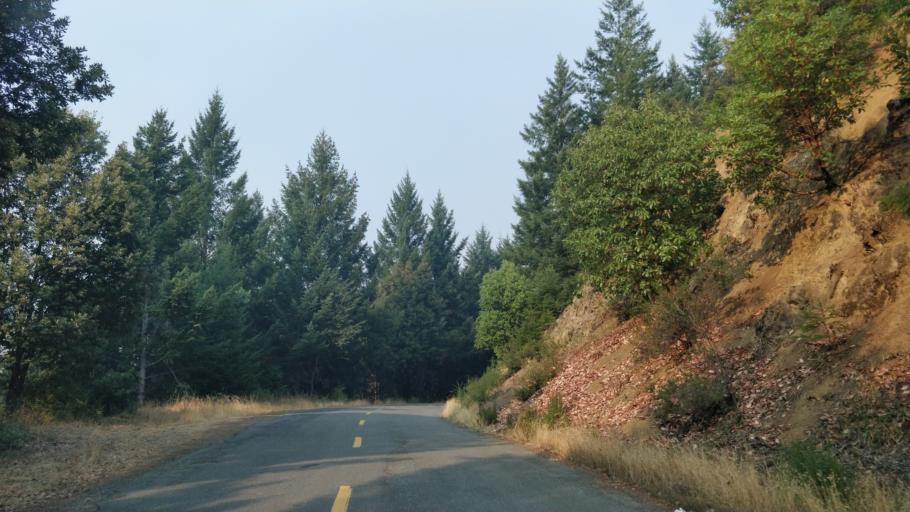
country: US
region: California
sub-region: Humboldt County
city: Rio Dell
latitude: 40.2626
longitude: -124.0948
